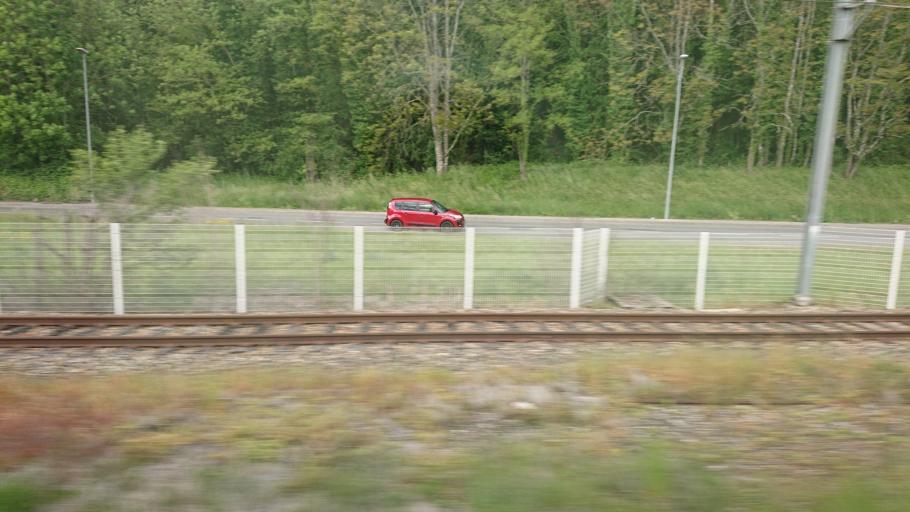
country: FR
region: Rhone-Alpes
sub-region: Departement de l'Ain
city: Culoz
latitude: 45.8435
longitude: 5.7748
